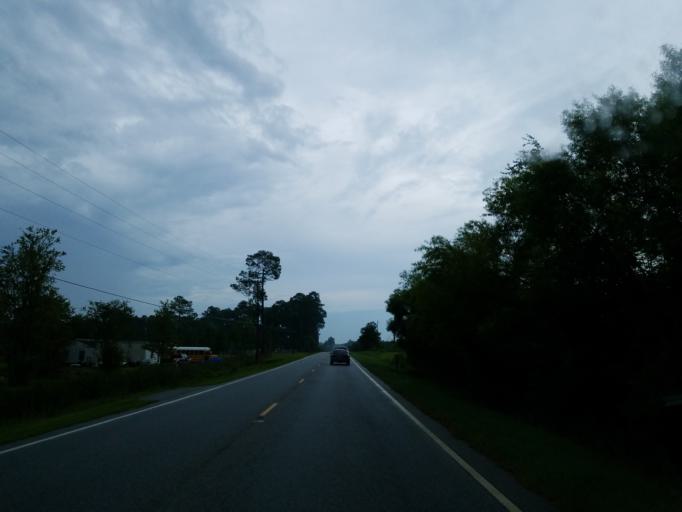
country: US
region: Georgia
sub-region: Berrien County
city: Ray City
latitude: 31.0607
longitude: -83.1565
